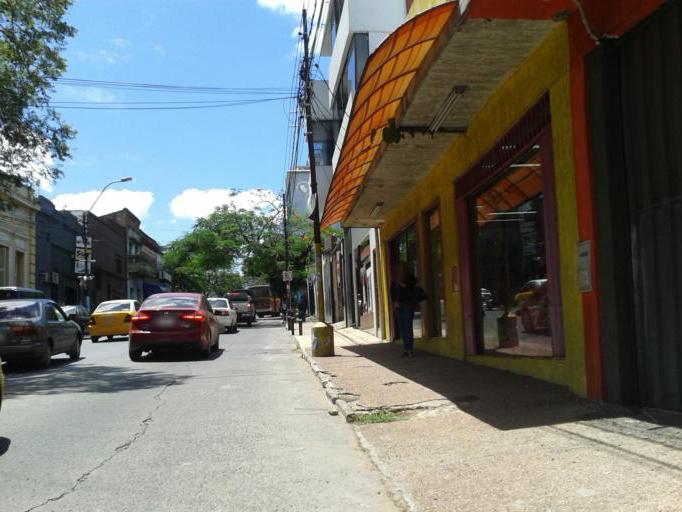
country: PY
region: Asuncion
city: Asuncion
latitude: -25.2903
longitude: -57.6269
